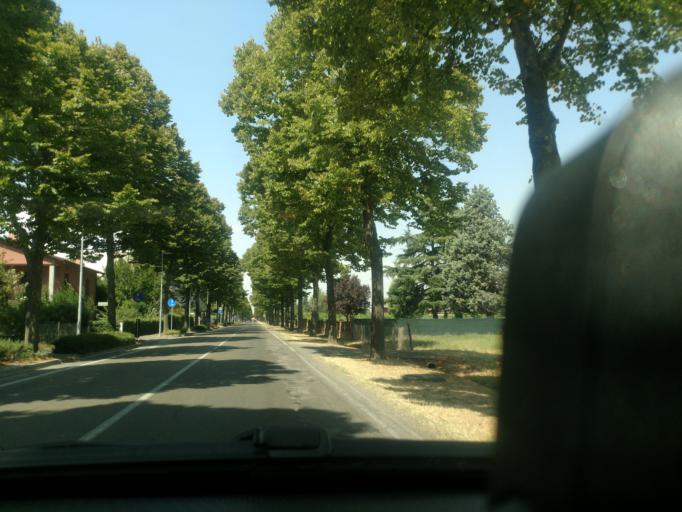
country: IT
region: Emilia-Romagna
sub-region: Provincia di Bologna
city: Castel Guelfo di Bologna
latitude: 44.4337
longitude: 11.6711
